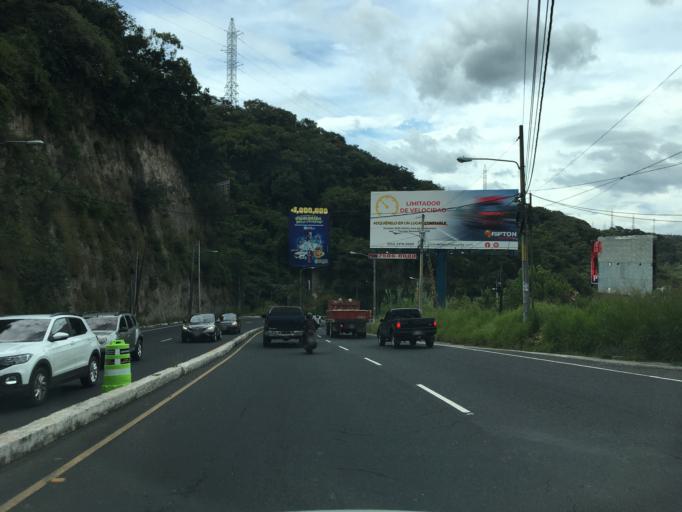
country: GT
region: Guatemala
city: Mixco
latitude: 14.5908
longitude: -90.5745
